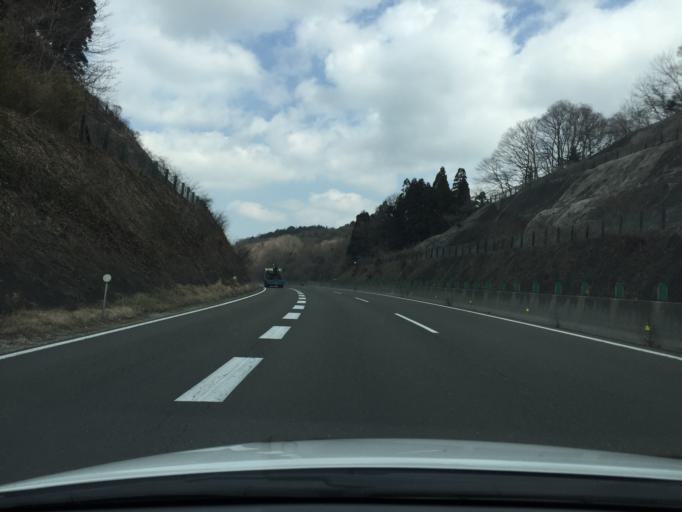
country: JP
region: Miyagi
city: Sendai
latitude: 38.2481
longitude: 140.8177
